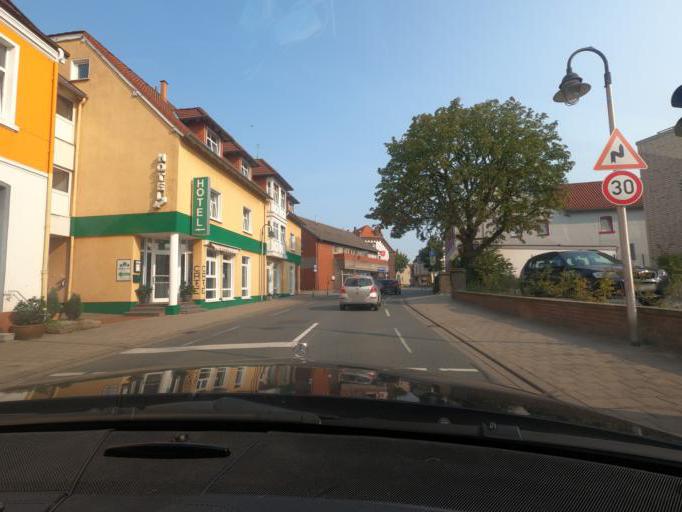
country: DE
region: North Rhine-Westphalia
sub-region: Regierungsbezirk Arnsberg
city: Hamm
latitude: 51.6301
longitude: 7.8565
